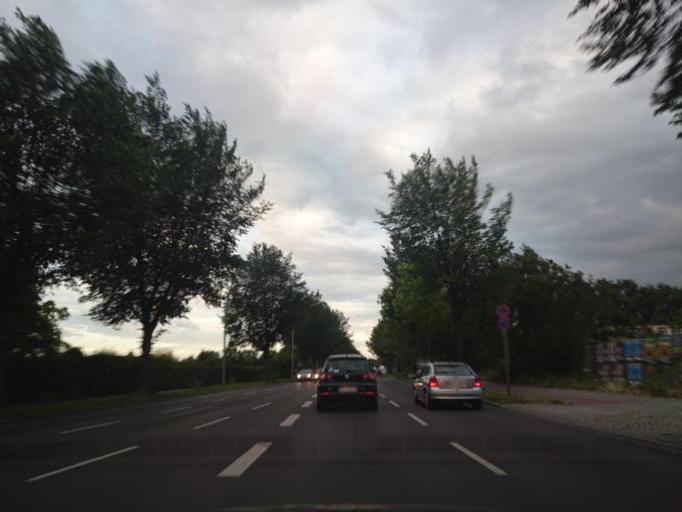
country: DE
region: Berlin
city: Adlershof
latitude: 52.4284
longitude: 13.5497
